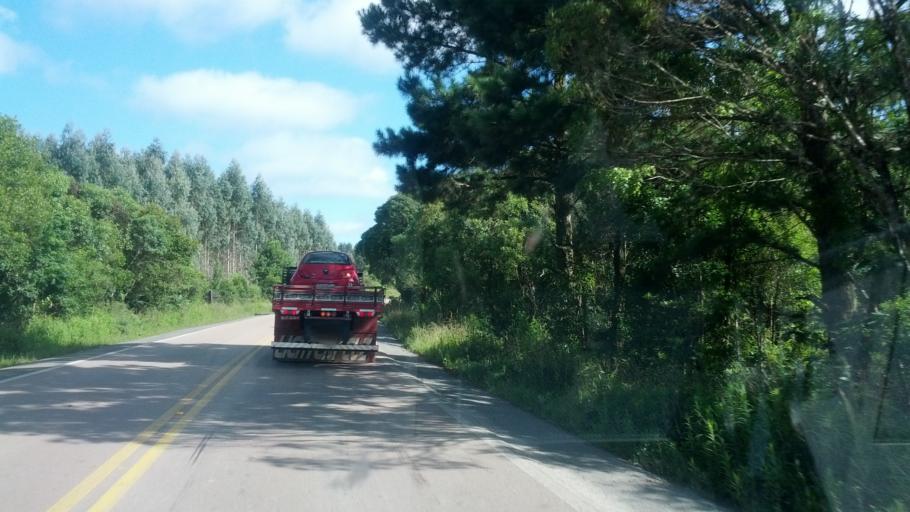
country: BR
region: Santa Catarina
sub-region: Otacilio Costa
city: Otacilio Costa
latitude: -27.4448
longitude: -50.1252
